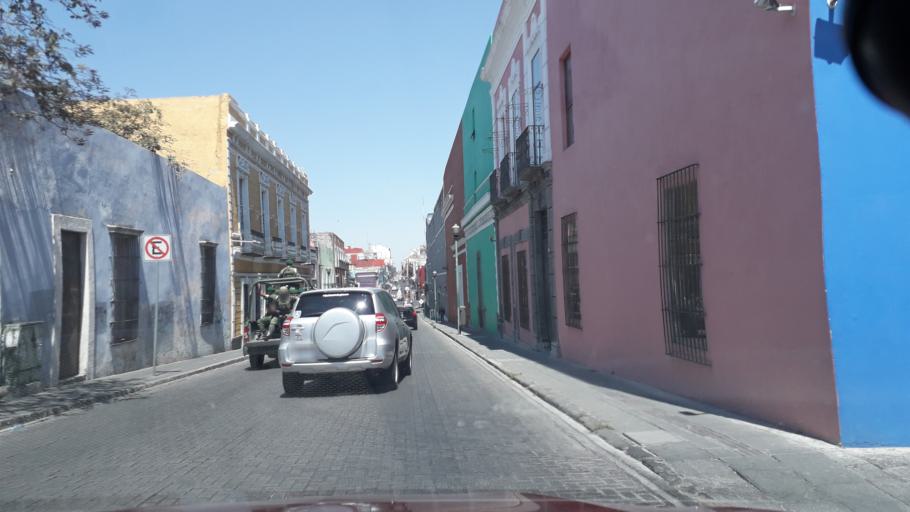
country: MX
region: Puebla
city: Puebla
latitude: 19.0415
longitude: -98.1910
